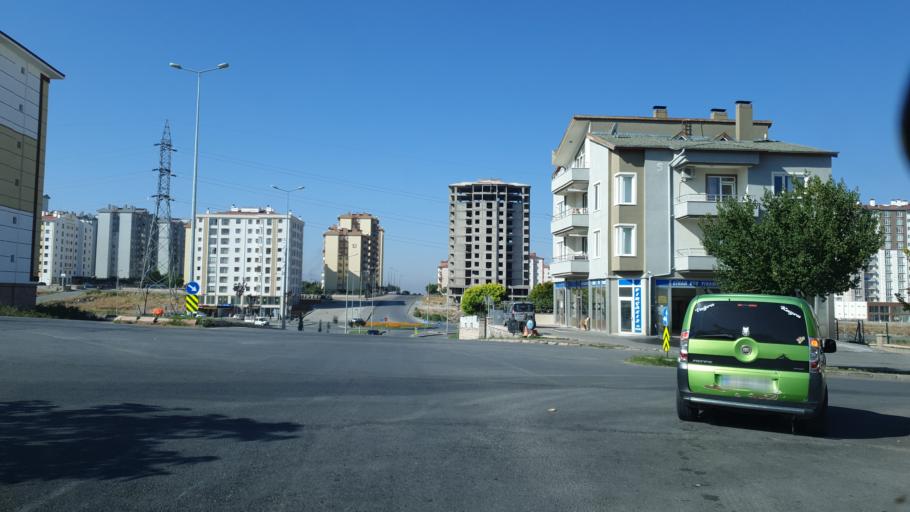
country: TR
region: Kayseri
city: Kocasinan
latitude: 38.7764
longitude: 35.5820
